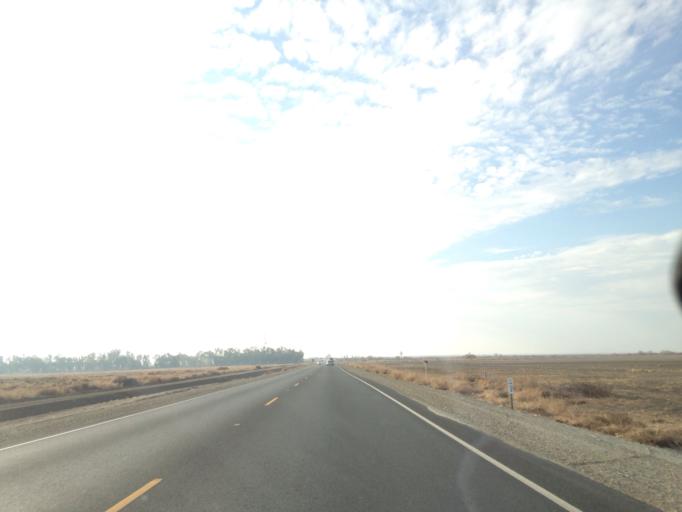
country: US
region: California
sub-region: Kern County
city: Lost Hills
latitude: 35.6162
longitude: -119.6368
